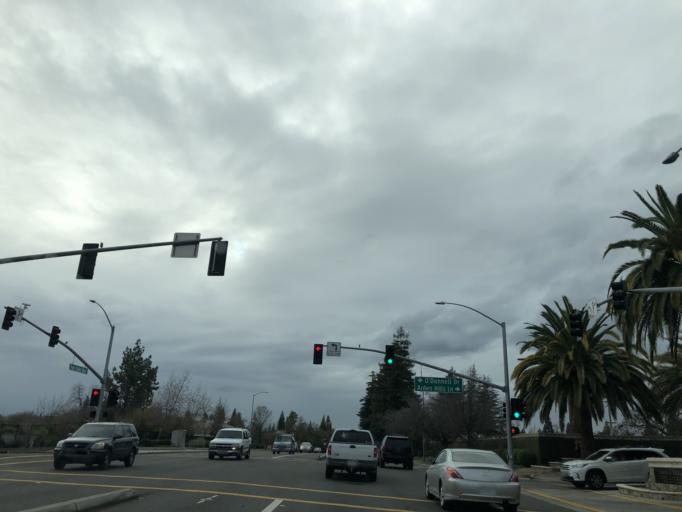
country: US
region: California
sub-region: Sacramento County
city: La Riviera
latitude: 38.5868
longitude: -121.3547
